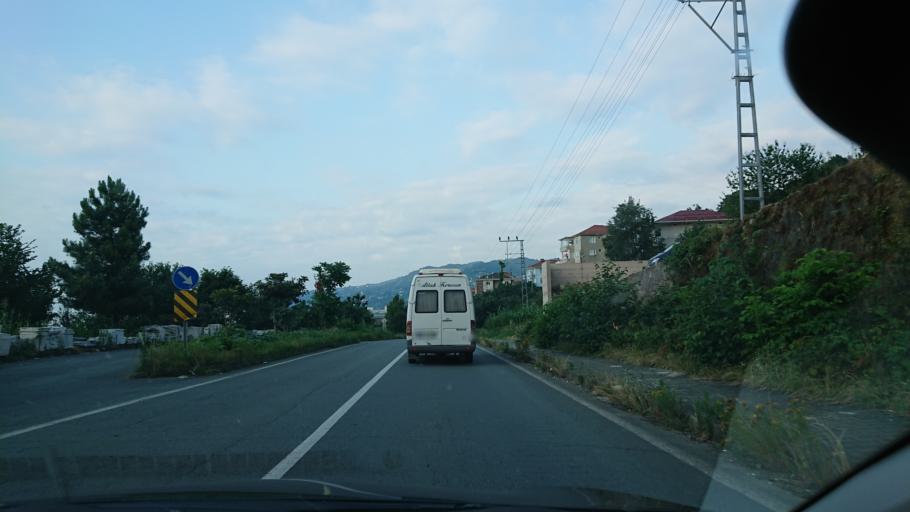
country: TR
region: Rize
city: Cayeli
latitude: 41.0791
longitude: 40.6990
